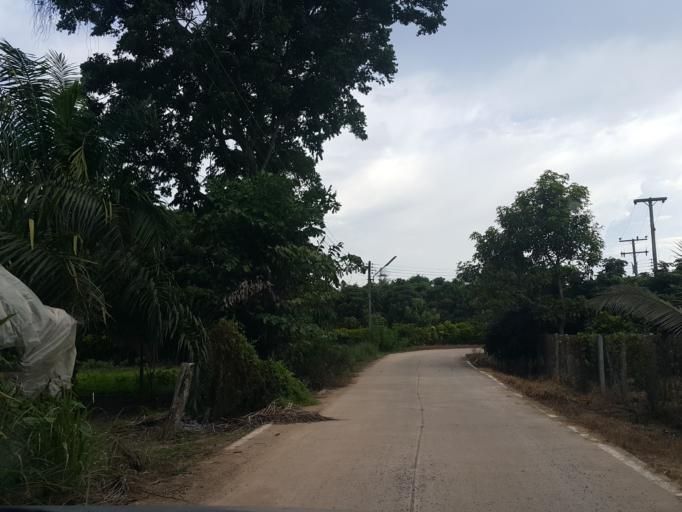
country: TH
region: Chiang Mai
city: Phrao
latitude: 19.3410
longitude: 99.1846
